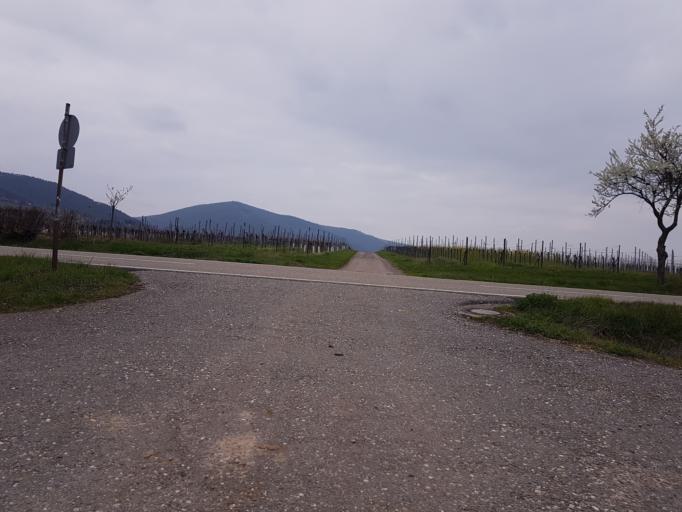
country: DE
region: Rheinland-Pfalz
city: Burrweiler
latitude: 49.2381
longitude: 8.0806
